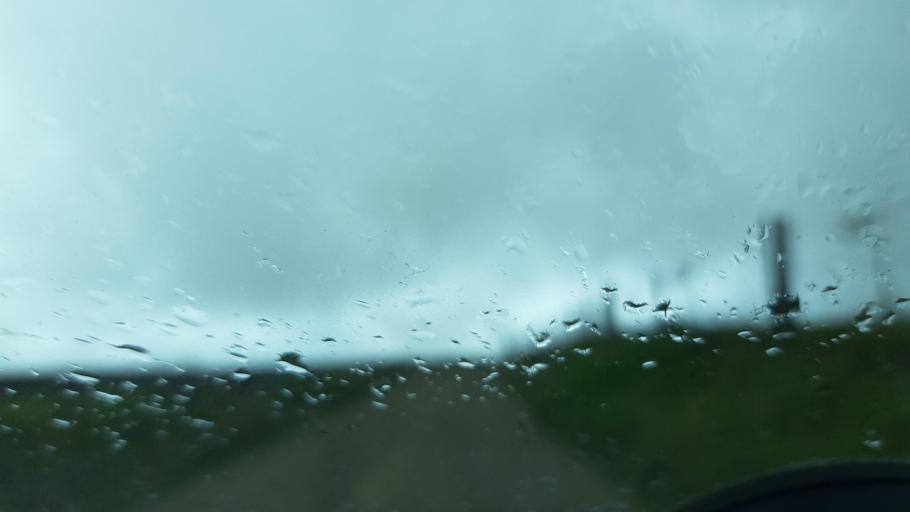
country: CO
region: Boyaca
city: Cucaita
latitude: 5.5213
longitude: -73.4399
